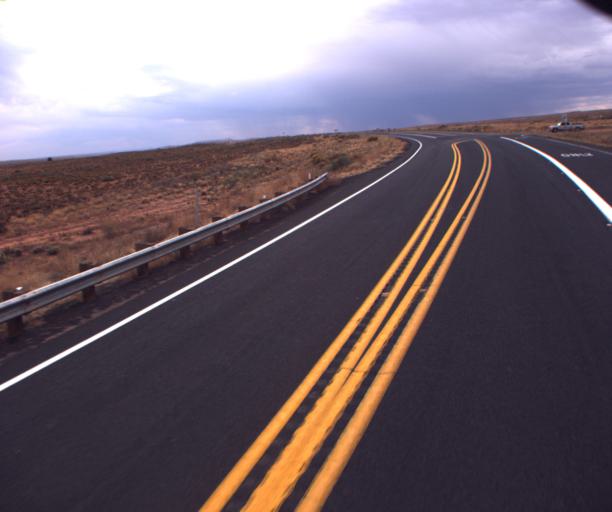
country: US
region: Arizona
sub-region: Coconino County
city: Kaibito
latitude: 36.3921
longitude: -110.8785
